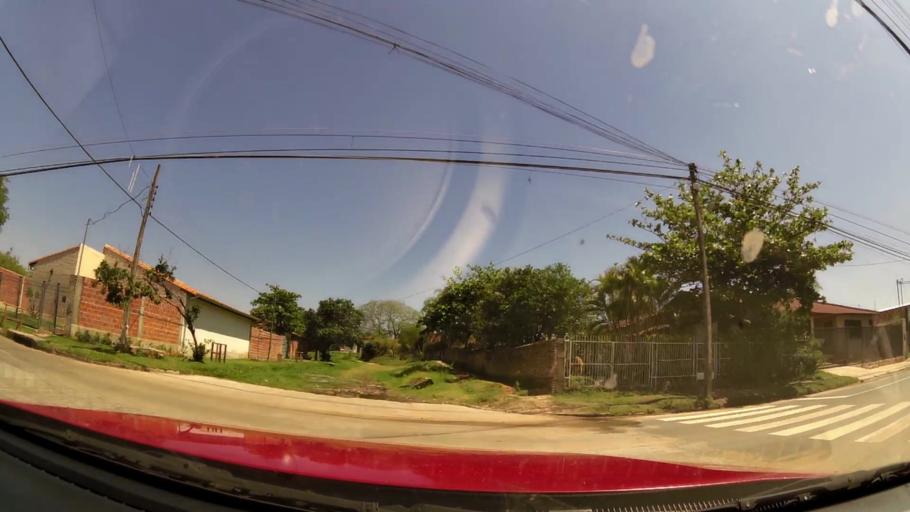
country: PY
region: Central
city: Colonia Mariano Roque Alonso
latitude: -25.2401
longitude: -57.5527
